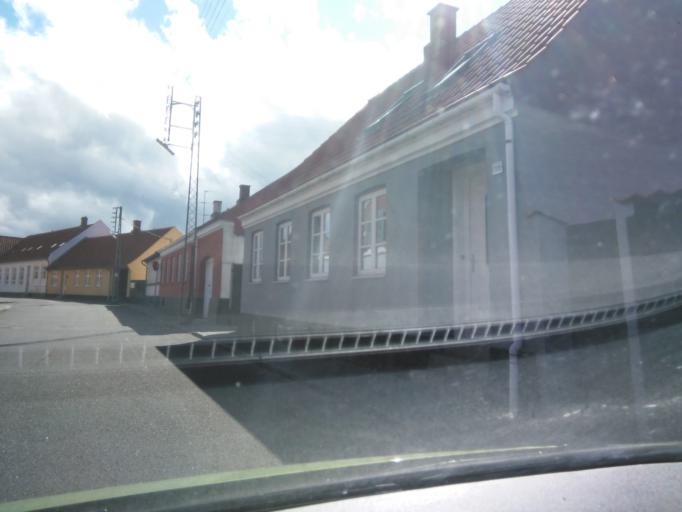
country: DK
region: Capital Region
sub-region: Bornholm Kommune
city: Nexo
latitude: 55.0622
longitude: 15.1294
